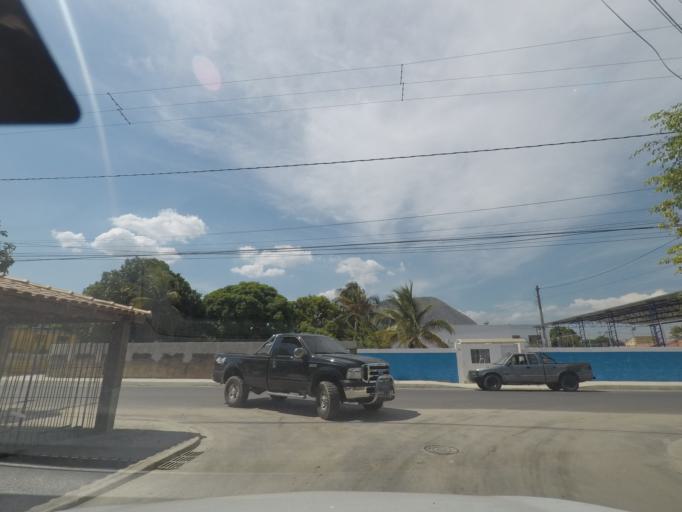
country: BR
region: Rio de Janeiro
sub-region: Marica
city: Marica
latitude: -22.9569
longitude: -42.9640
